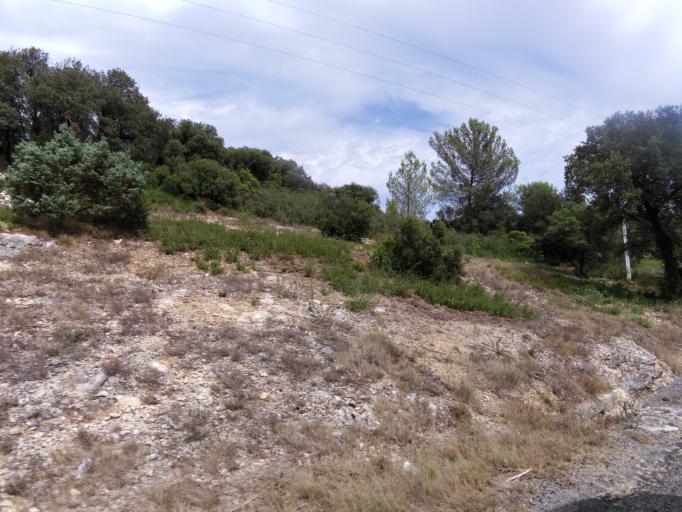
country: FR
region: Languedoc-Roussillon
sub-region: Departement du Gard
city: Congenies
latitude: 43.8080
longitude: 4.1506
